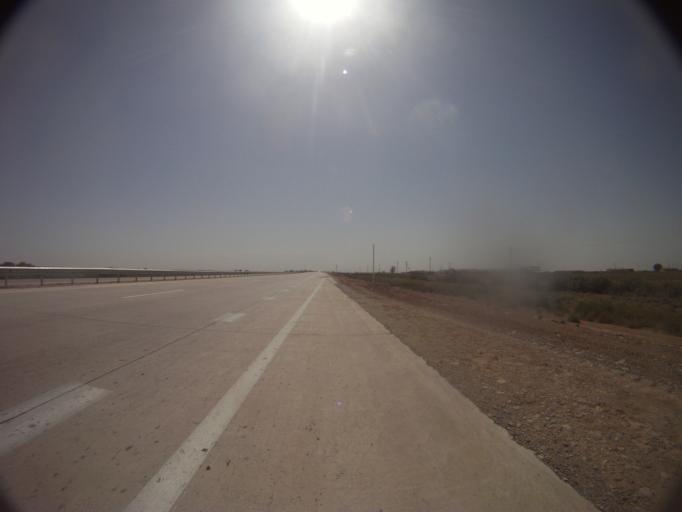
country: KZ
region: Ongtustik Qazaqstan
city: Khantaghy
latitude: 43.1268
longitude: 68.5951
